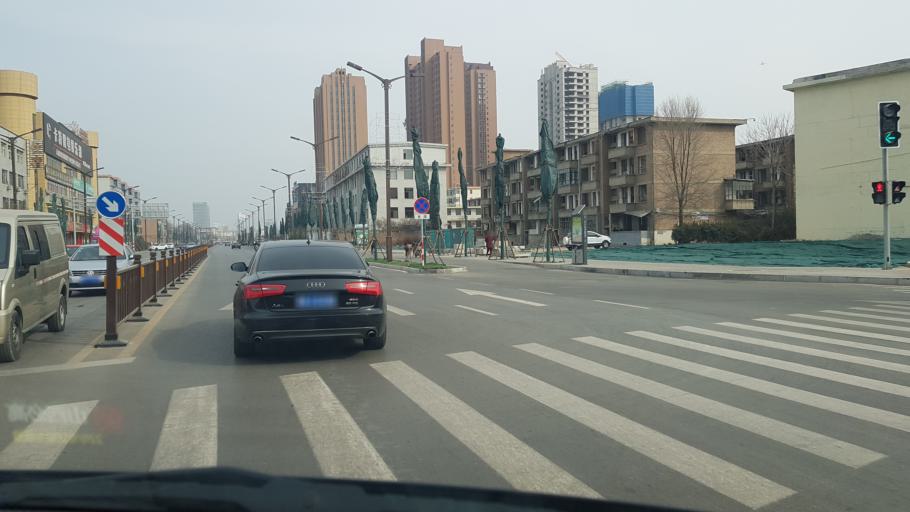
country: CN
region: Shanxi Sheng
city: Yuci
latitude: 37.6896
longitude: 112.7214
